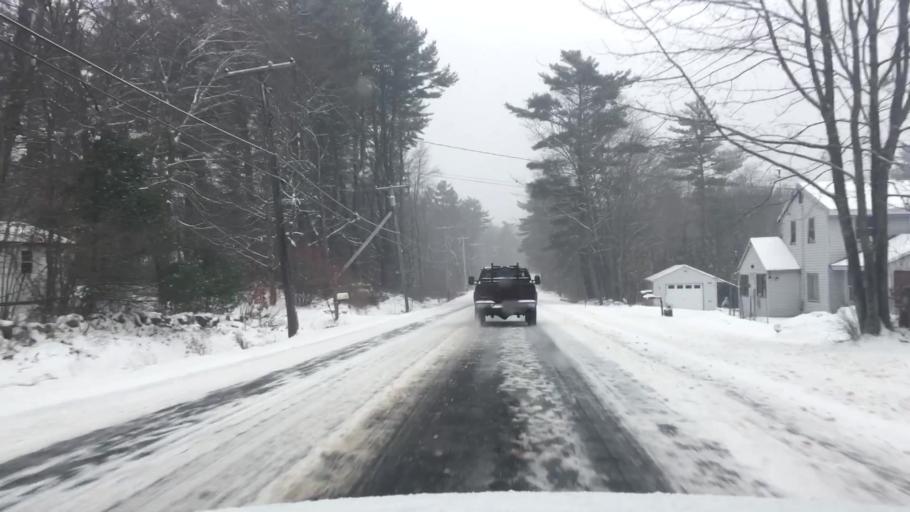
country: US
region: Maine
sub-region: Cumberland County
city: Cumberland Center
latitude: 43.8309
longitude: -70.3192
